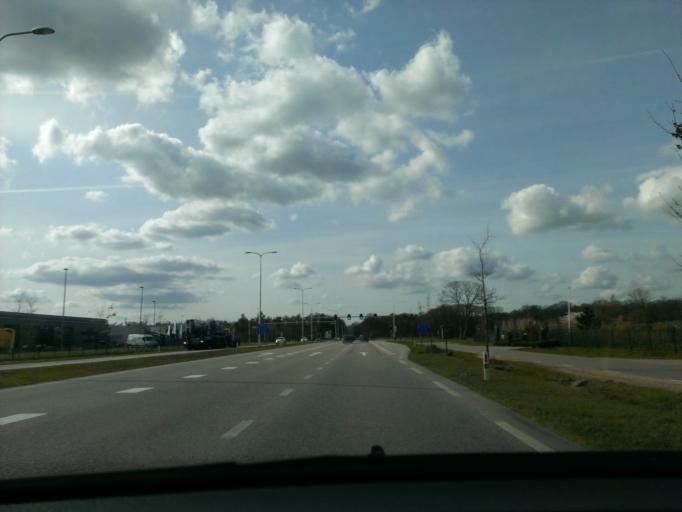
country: NL
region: Gelderland
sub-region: Gemeente Apeldoorn
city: Apeldoorn
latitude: 52.2010
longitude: 6.0377
